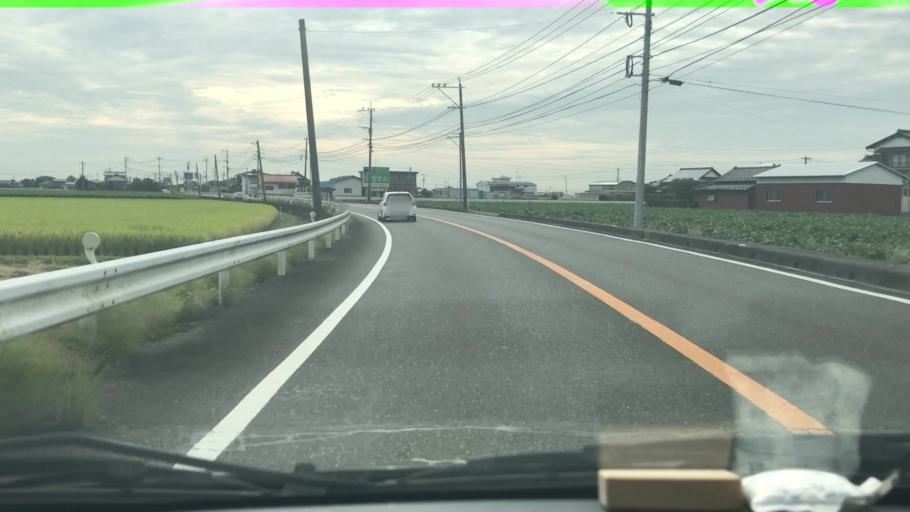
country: JP
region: Saga Prefecture
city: Takeocho-takeo
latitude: 33.1998
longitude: 130.0986
